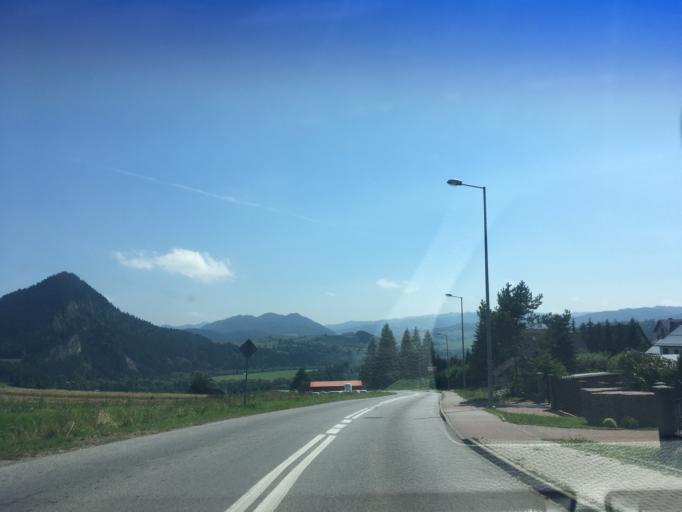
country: PL
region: Lesser Poland Voivodeship
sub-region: Powiat nowotarski
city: Krosnica
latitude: 49.4093
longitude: 20.3529
